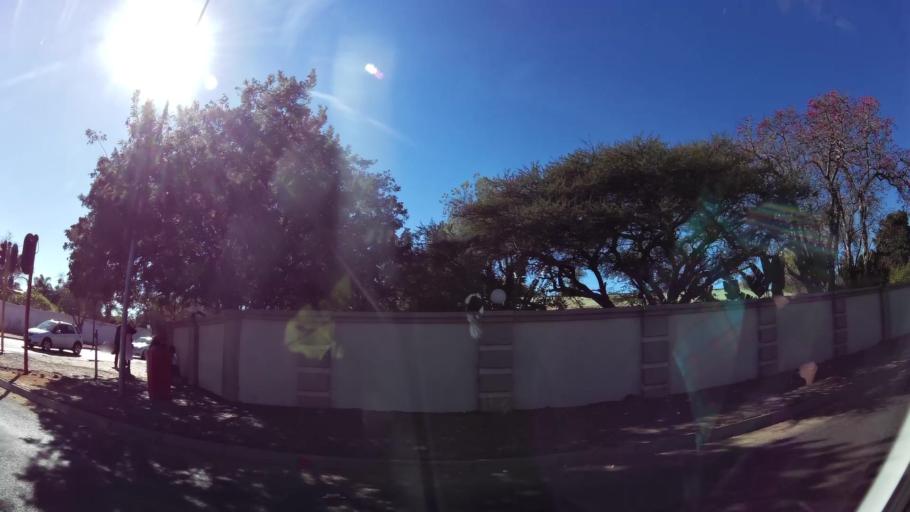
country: ZA
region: Limpopo
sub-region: Capricorn District Municipality
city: Polokwane
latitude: -23.9031
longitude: 29.4728
